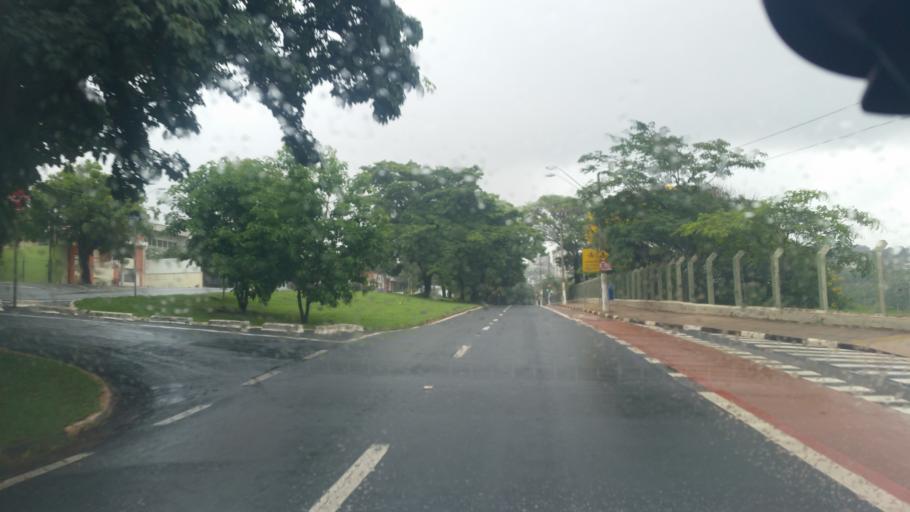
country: BR
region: Sao Paulo
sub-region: Campinas
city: Campinas
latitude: -22.8777
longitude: -47.0587
